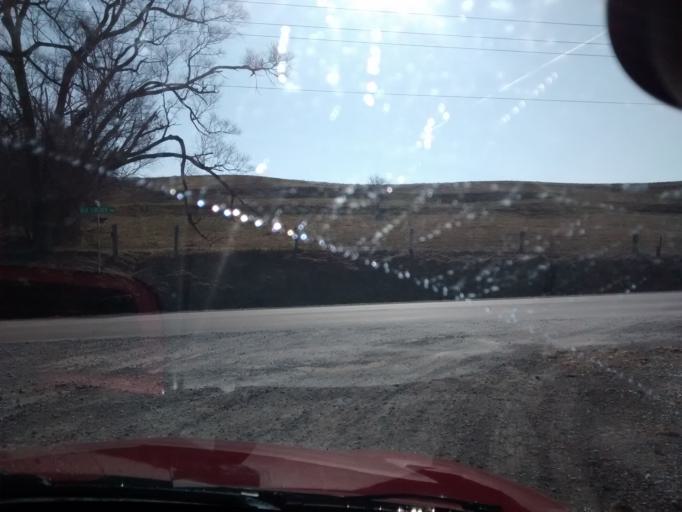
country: US
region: Iowa
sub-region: Pottawattamie County
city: Carter Lake
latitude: 41.3905
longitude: -95.8424
